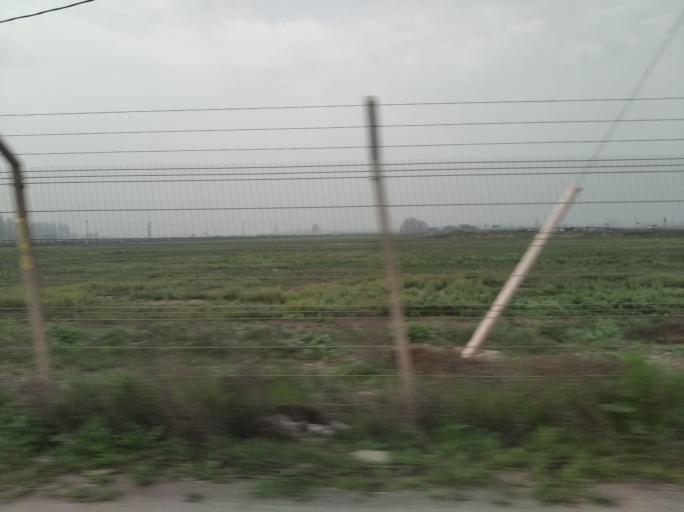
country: CL
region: Santiago Metropolitan
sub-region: Provincia de Chacabuco
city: Lampa
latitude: -33.3645
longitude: -70.8012
